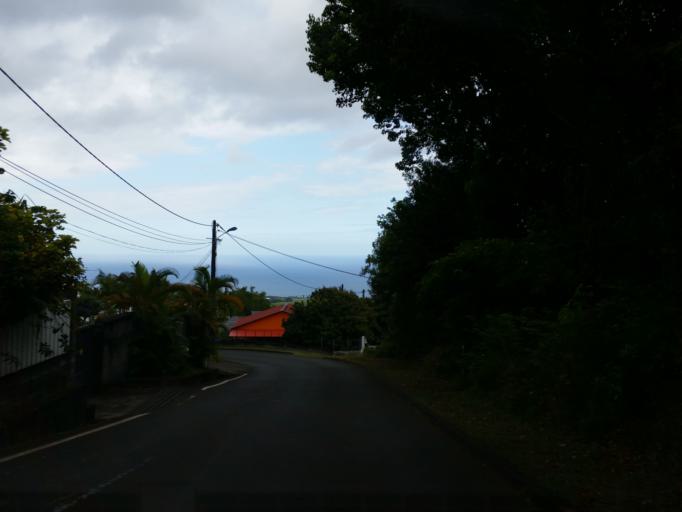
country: RE
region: Reunion
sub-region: Reunion
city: Sainte-Marie
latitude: -20.9345
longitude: 55.5419
